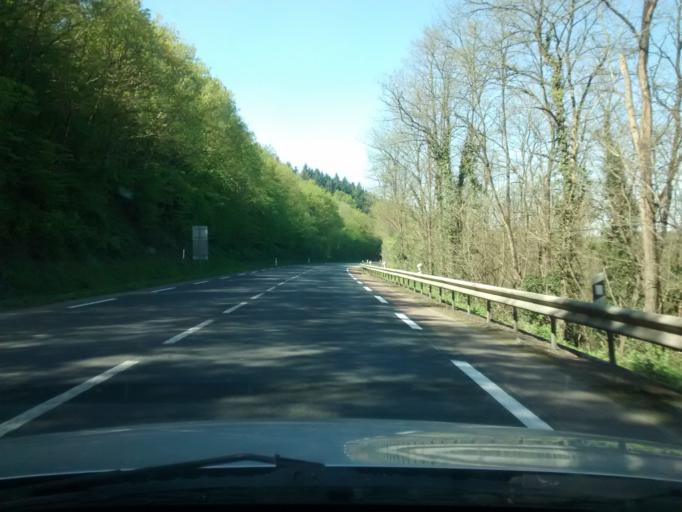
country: FR
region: Pays de la Loire
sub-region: Departement de la Sarthe
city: Brulon
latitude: 48.0267
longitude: -0.2451
